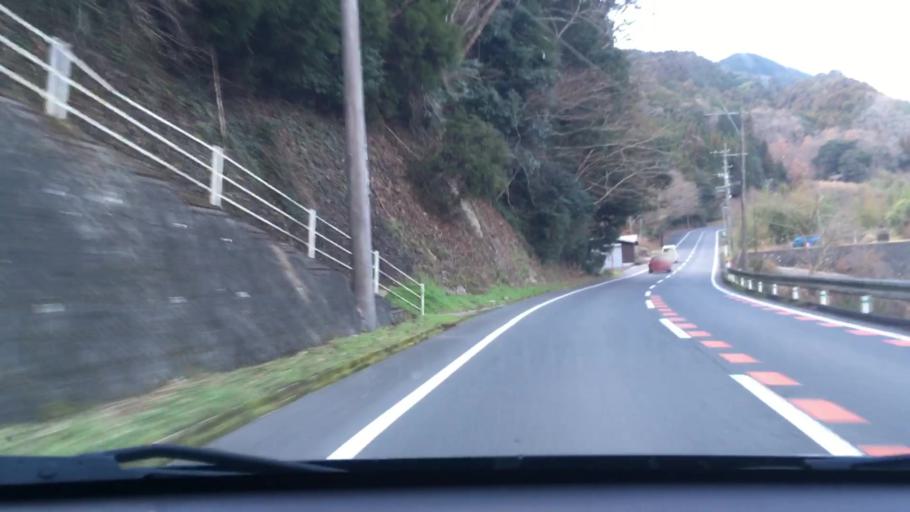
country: JP
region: Oita
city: Bungo-Takada-shi
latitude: 33.4690
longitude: 131.3866
